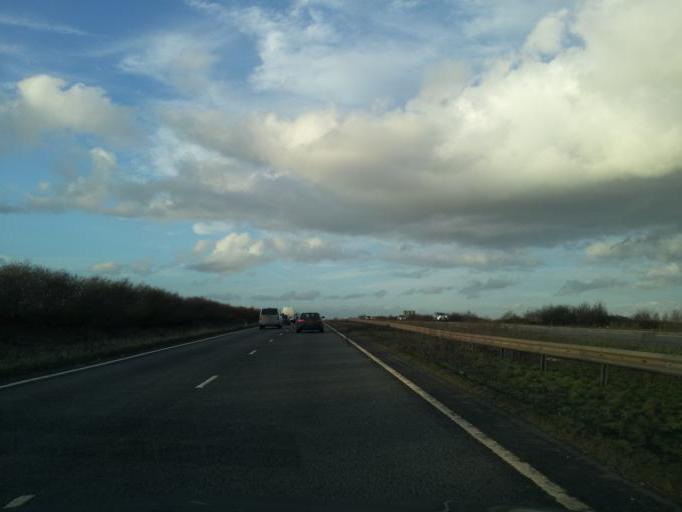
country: GB
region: England
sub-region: District of Rutland
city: Greetham
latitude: 52.7824
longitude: -0.6111
